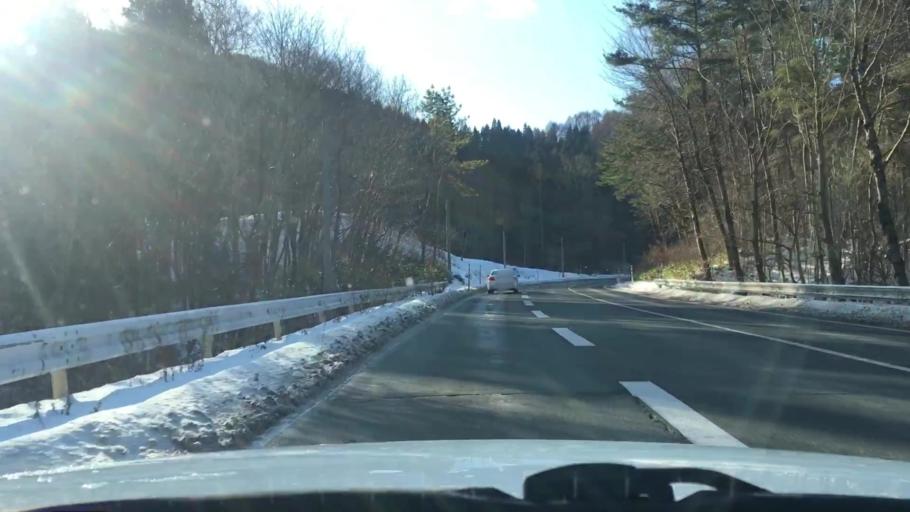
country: JP
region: Iwate
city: Morioka-shi
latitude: 39.6679
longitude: 141.3324
